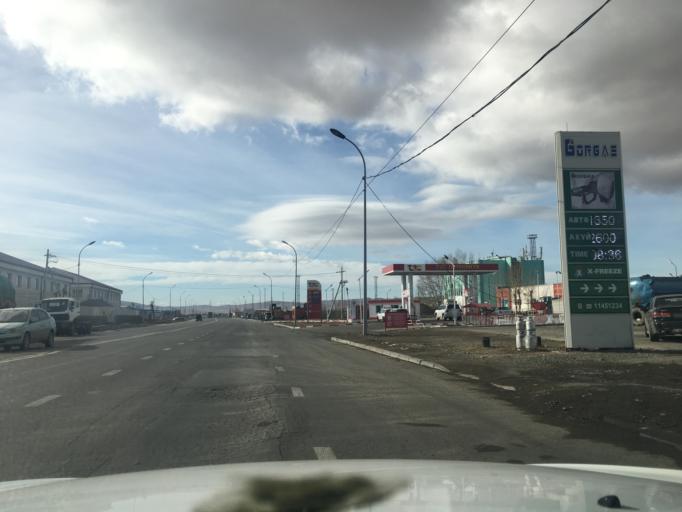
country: MN
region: Ulaanbaatar
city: Ulaanbaatar
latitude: 47.9056
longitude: 106.7633
